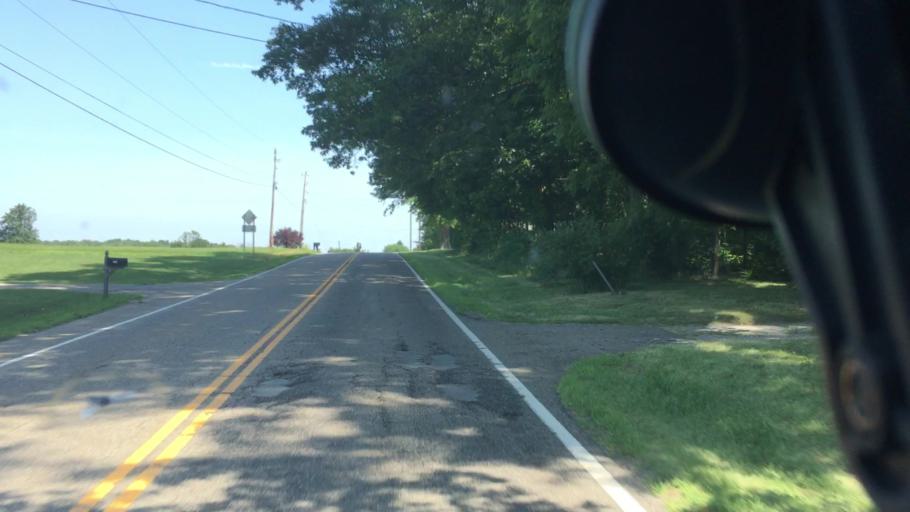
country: US
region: Ohio
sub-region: Columbiana County
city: Lisbon
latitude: 40.8025
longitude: -80.8585
